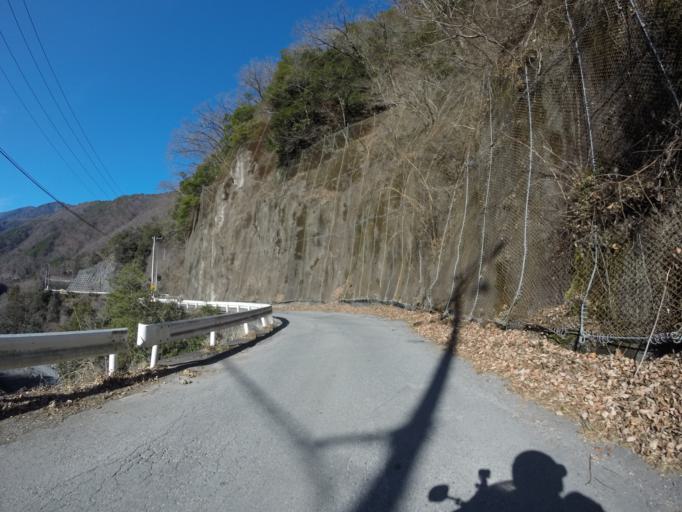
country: JP
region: Yamanashi
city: Ryuo
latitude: 35.4124
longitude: 138.3544
